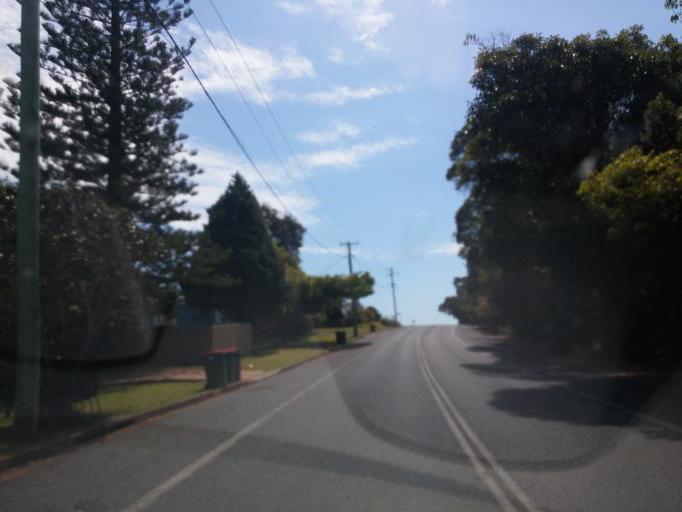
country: AU
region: New South Wales
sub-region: Port Macquarie-Hastings
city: Port Macquarie
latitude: -31.4538
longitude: 152.9296
